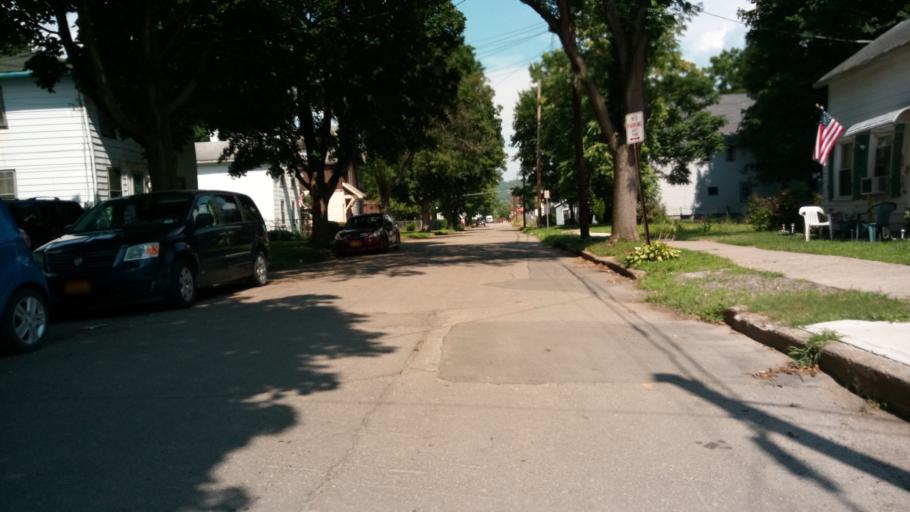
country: US
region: New York
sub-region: Chemung County
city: Elmira
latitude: 42.0938
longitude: -76.8143
